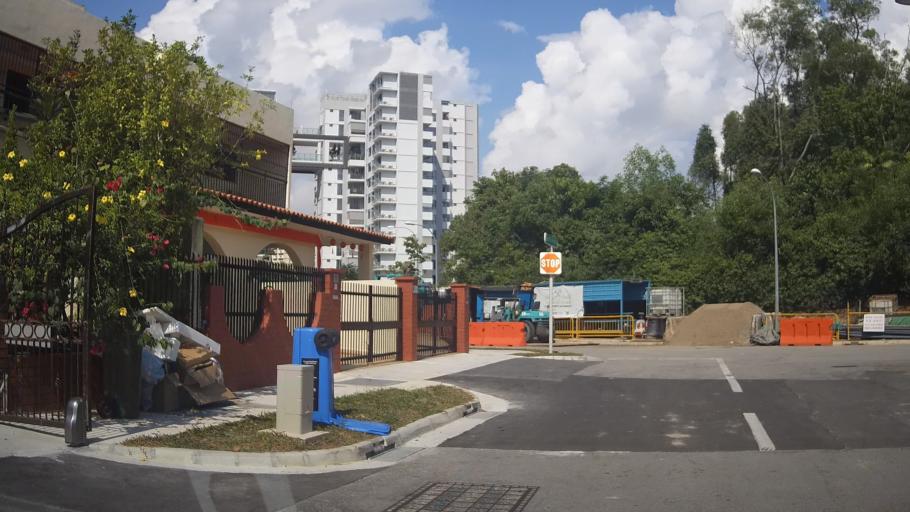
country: MY
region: Johor
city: Kampung Pasir Gudang Baru
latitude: 1.3821
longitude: 103.9423
